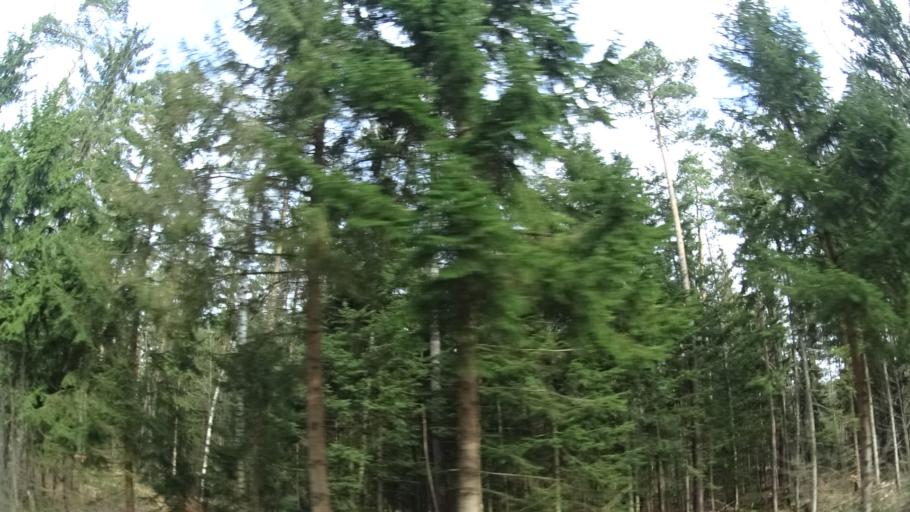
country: DE
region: Bavaria
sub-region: Regierungsbezirk Mittelfranken
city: Winkelhaid
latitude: 49.4091
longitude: 11.2894
